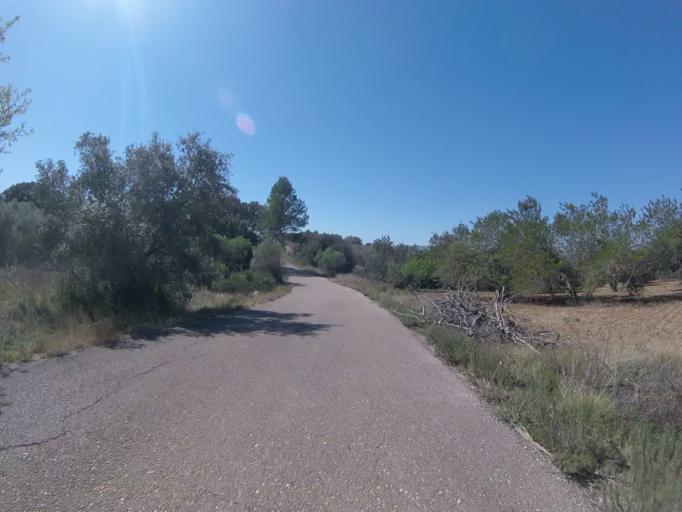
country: ES
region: Valencia
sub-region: Provincia de Castello
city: Cuevas de Vinroma
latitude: 40.3830
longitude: 0.1560
